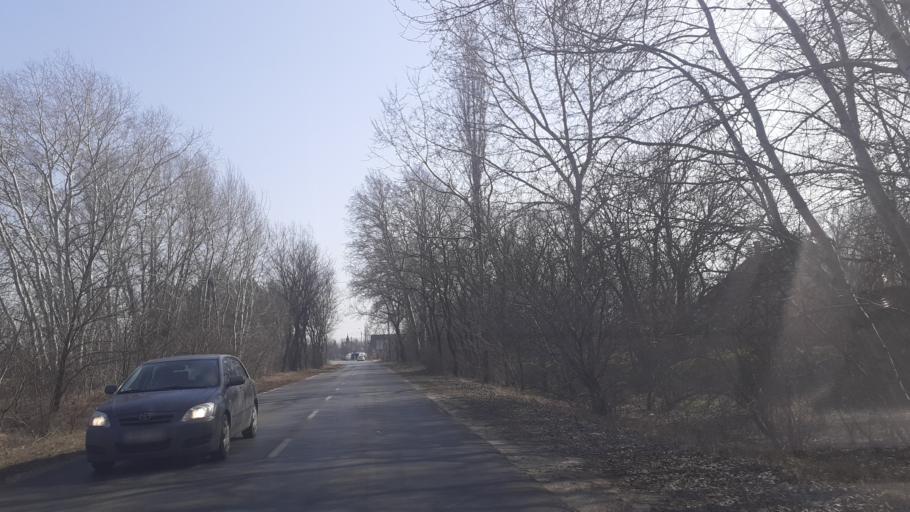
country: HU
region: Bacs-Kiskun
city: Lajosmizse
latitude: 46.9794
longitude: 19.5705
